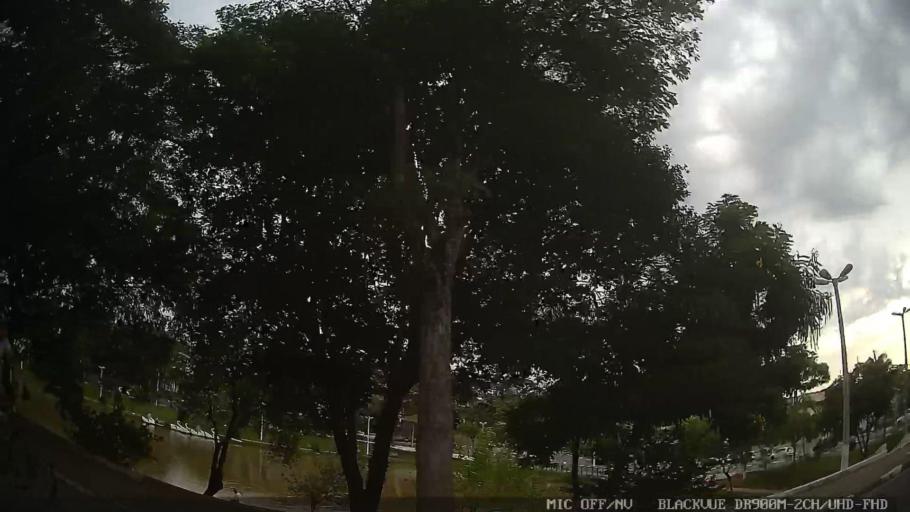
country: BR
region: Sao Paulo
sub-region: Atibaia
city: Atibaia
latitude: -23.1196
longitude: -46.5503
